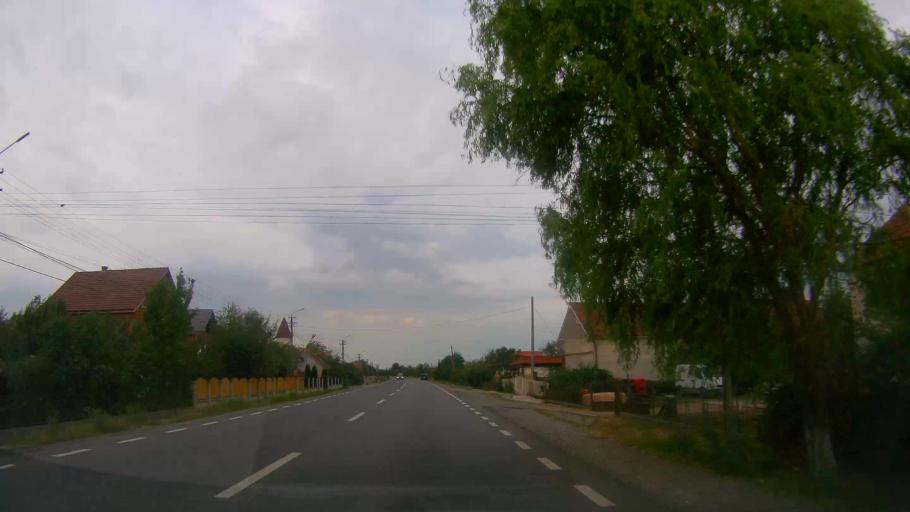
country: RO
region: Satu Mare
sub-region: Comuna Agris
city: Agris
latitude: 47.8702
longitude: 23.0147
